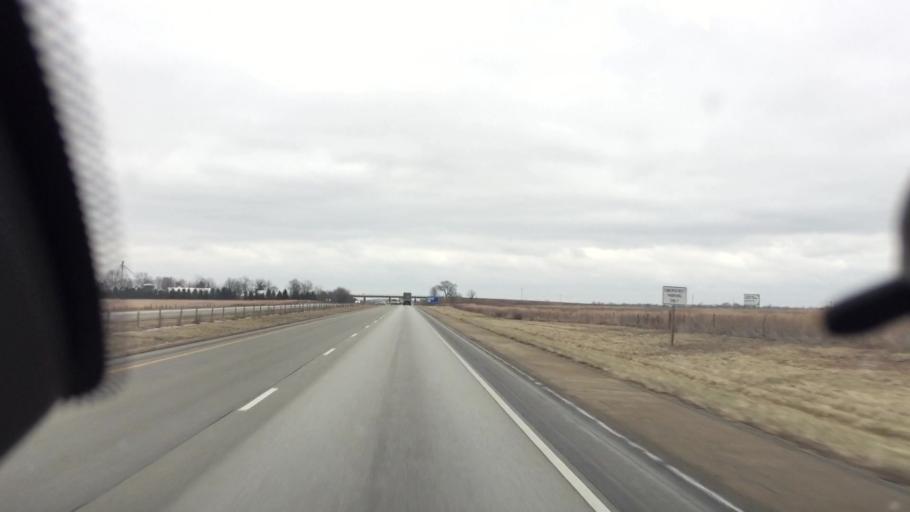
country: US
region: Illinois
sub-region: Vermilion County
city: Oakwood
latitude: 40.1264
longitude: -87.8172
